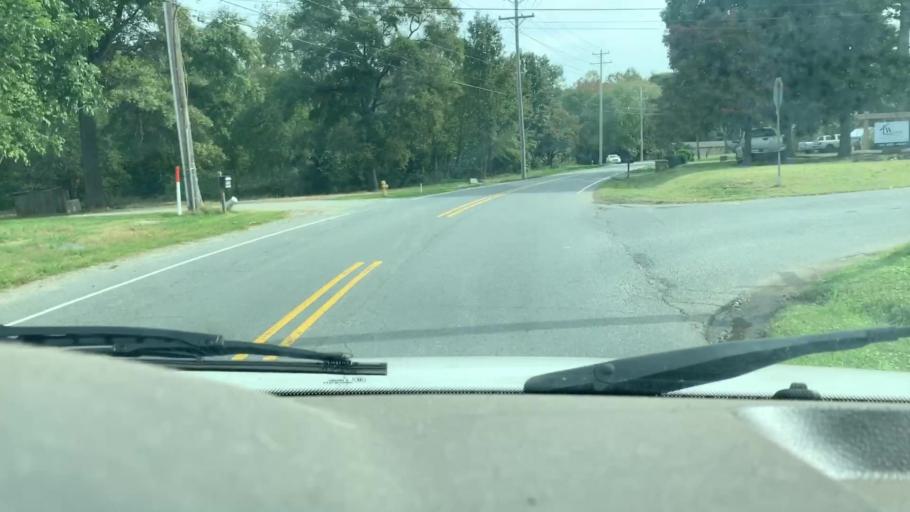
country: US
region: North Carolina
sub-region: Mecklenburg County
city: Huntersville
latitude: 35.4208
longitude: -80.8380
